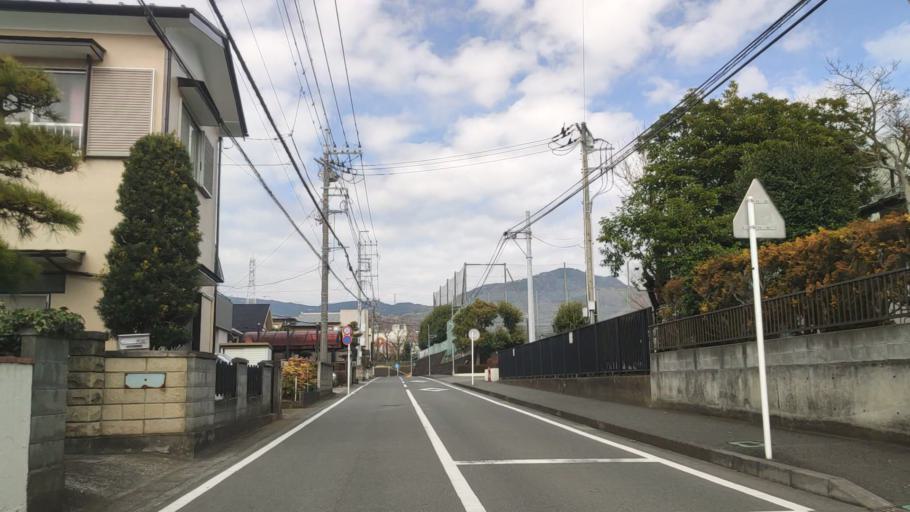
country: JP
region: Kanagawa
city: Hadano
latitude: 35.3784
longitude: 139.2360
